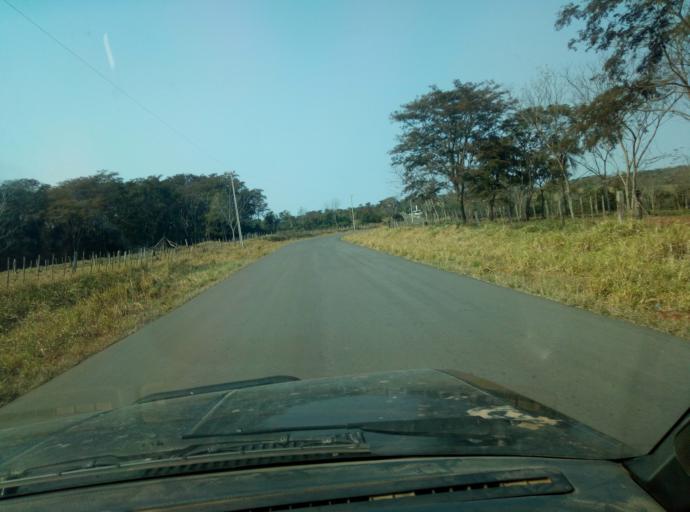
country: PY
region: Caaguazu
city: Carayao
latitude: -25.1962
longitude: -56.3090
